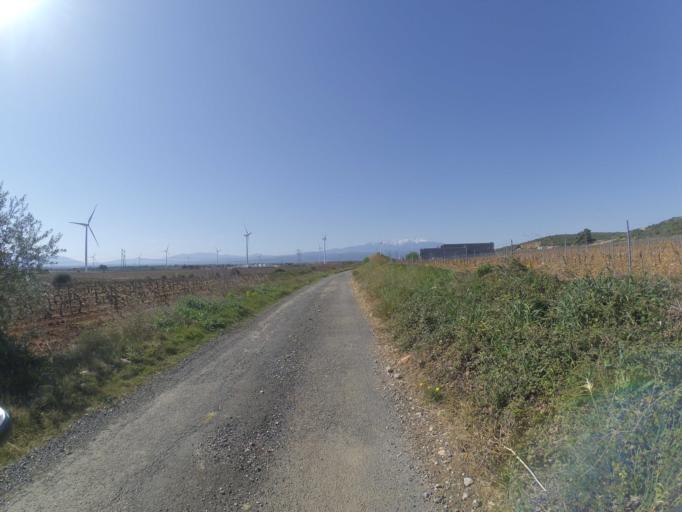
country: FR
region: Languedoc-Roussillon
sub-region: Departement des Pyrenees-Orientales
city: Baixas
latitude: 42.7329
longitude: 2.7774
